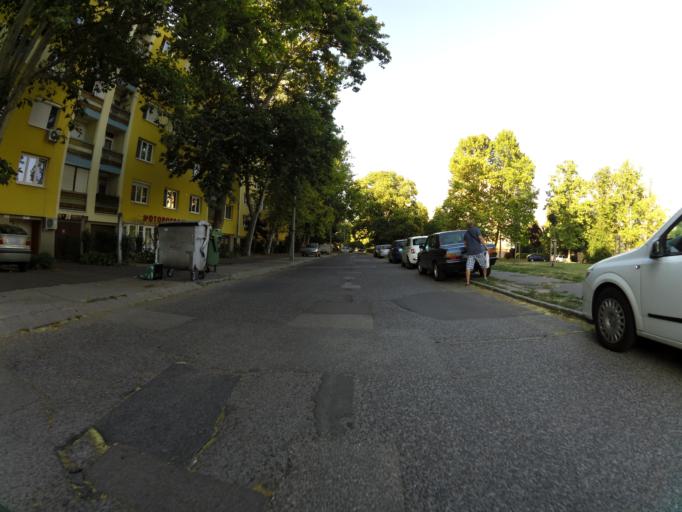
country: HU
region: Csongrad
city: Szeged
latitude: 46.2628
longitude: 20.1675
